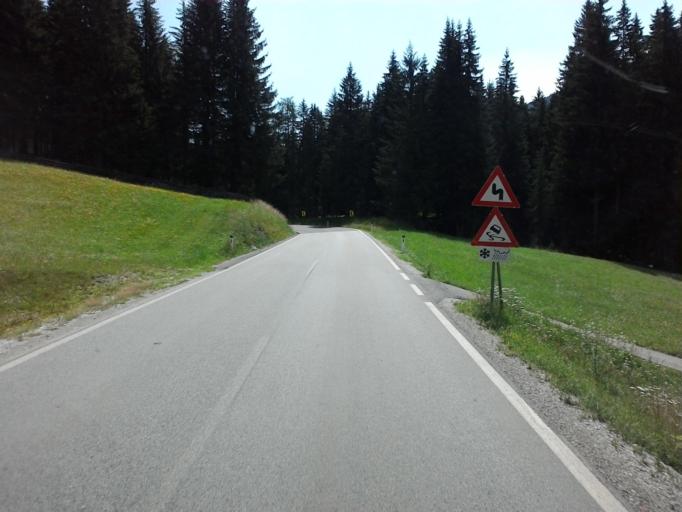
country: AT
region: Tyrol
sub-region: Politischer Bezirk Lienz
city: Obertilliach
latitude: 46.7141
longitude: 12.5743
